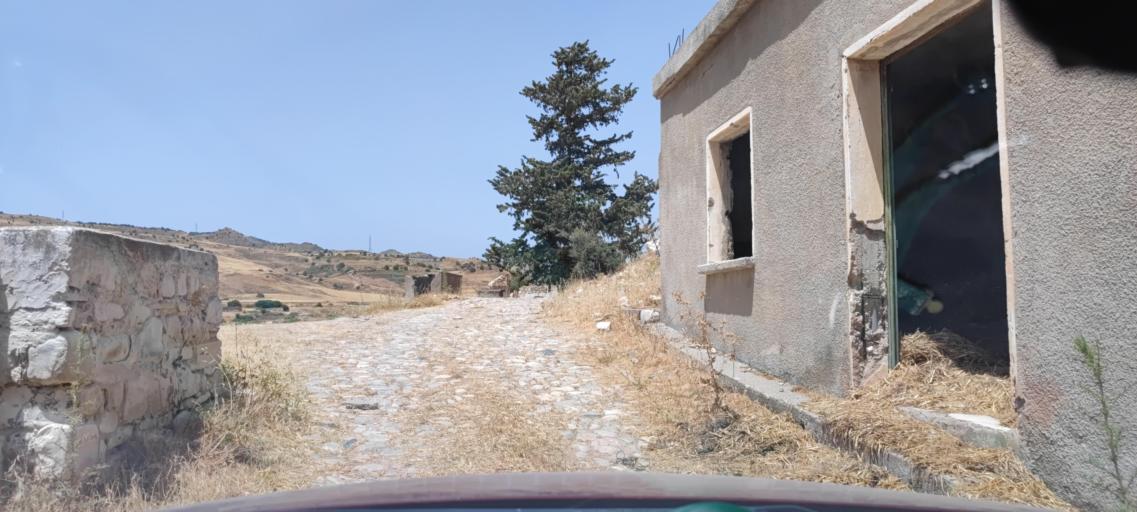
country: CY
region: Limassol
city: Pissouri
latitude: 34.7336
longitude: 32.6025
